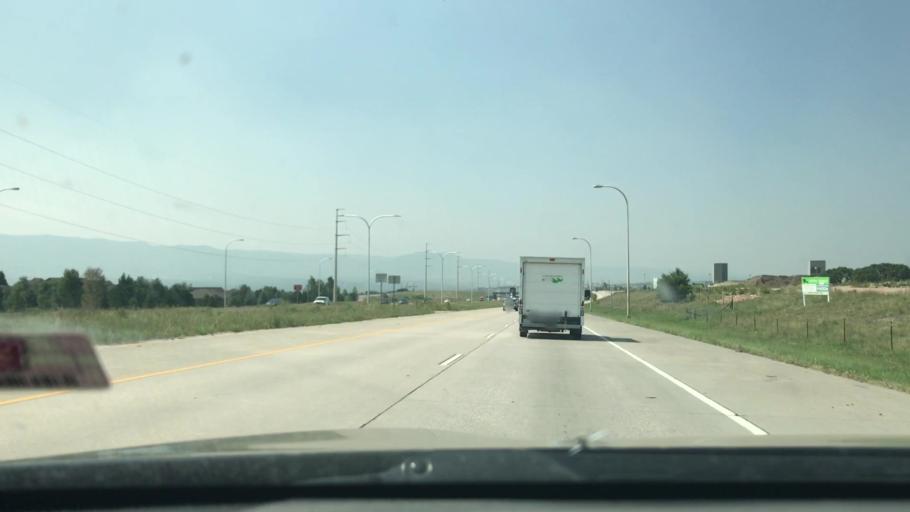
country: US
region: Colorado
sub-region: El Paso County
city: Black Forest
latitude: 38.9797
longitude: -104.7576
